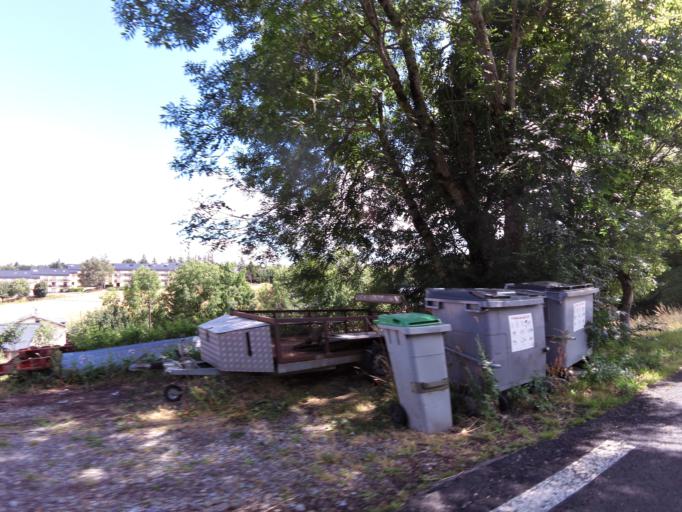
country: FR
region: Languedoc-Roussillon
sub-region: Departement du Gard
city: Valleraugue
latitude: 44.0943
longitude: 3.5472
